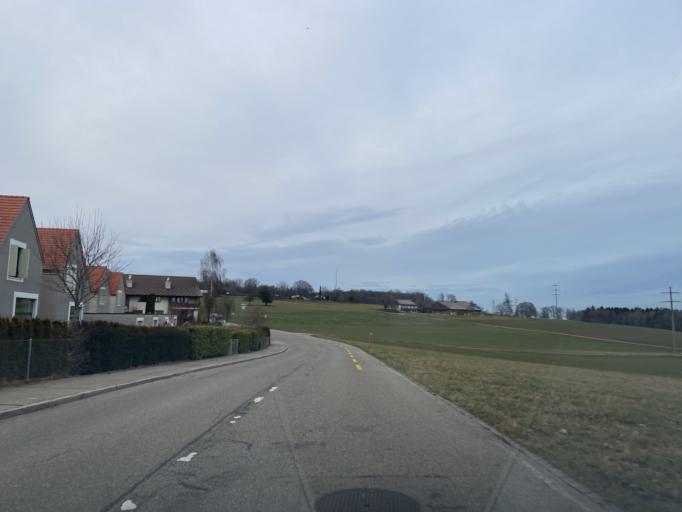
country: CH
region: Zurich
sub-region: Bezirk Winterthur
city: Brutten
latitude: 47.4714
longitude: 8.6833
